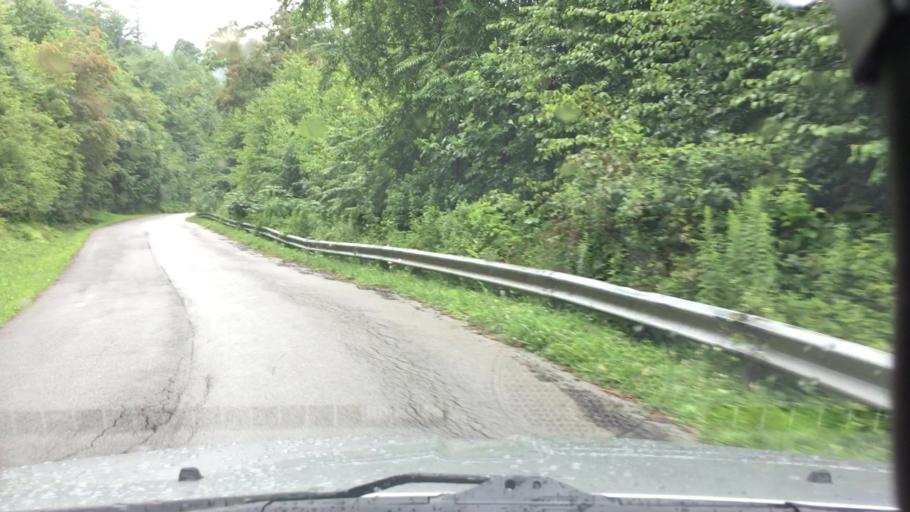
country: US
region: North Carolina
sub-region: Madison County
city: Mars Hill
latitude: 35.9505
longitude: -82.5134
